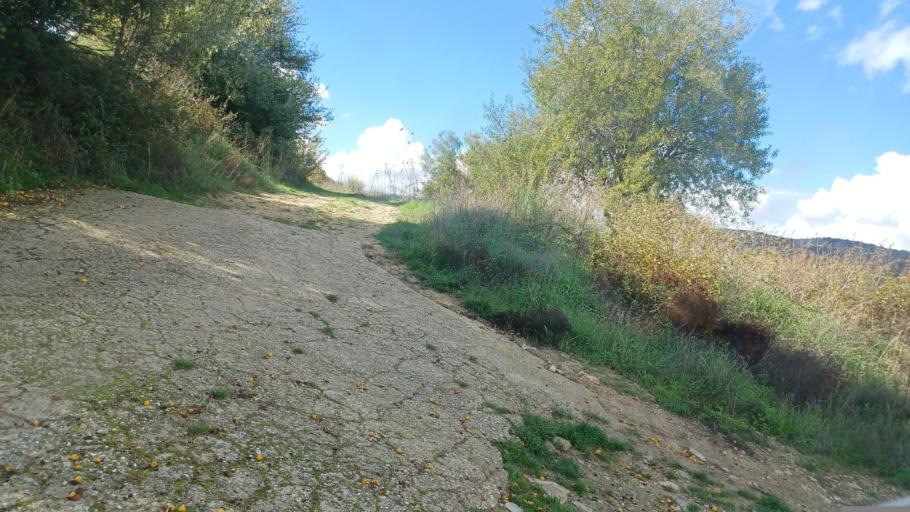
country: CY
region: Pafos
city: Mesogi
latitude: 34.8359
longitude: 32.5500
